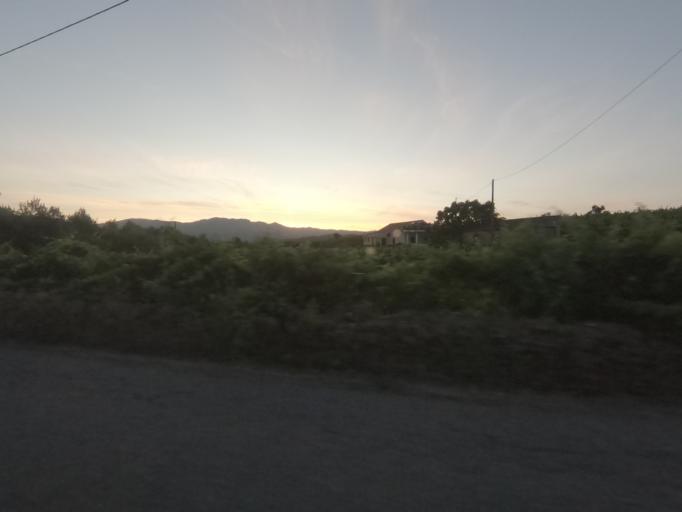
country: PT
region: Vila Real
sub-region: Peso da Regua
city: Peso da Regua
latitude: 41.1949
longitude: -7.7068
